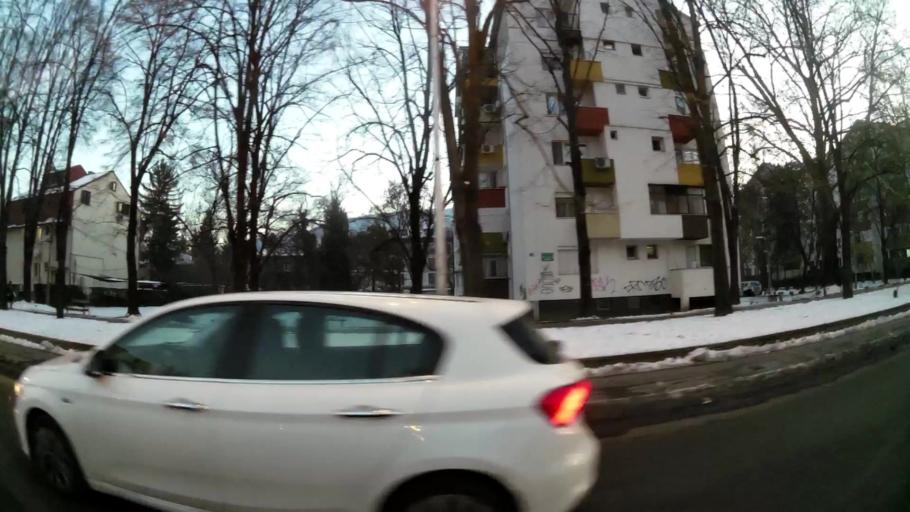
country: MK
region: Karpos
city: Skopje
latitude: 42.0011
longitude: 21.4092
